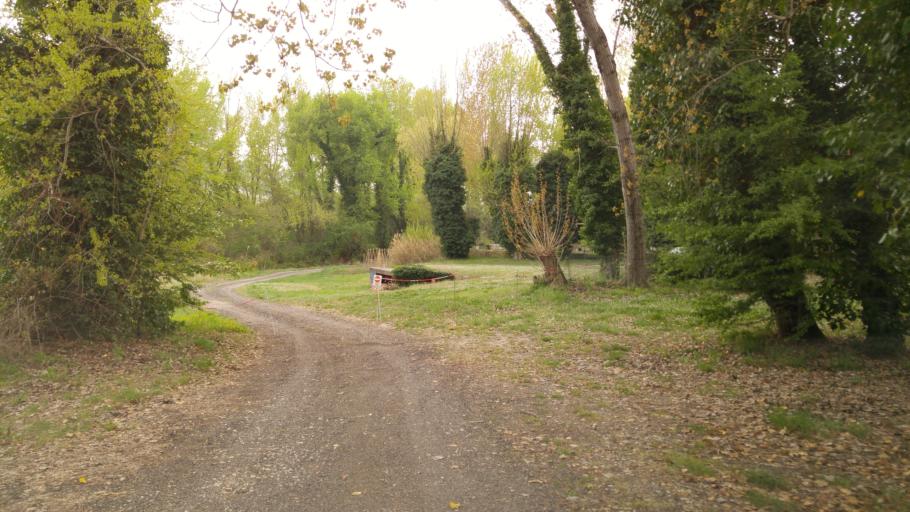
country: IT
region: The Marches
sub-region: Provincia di Pesaro e Urbino
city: Bellocchi
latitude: 43.7704
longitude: 12.9887
